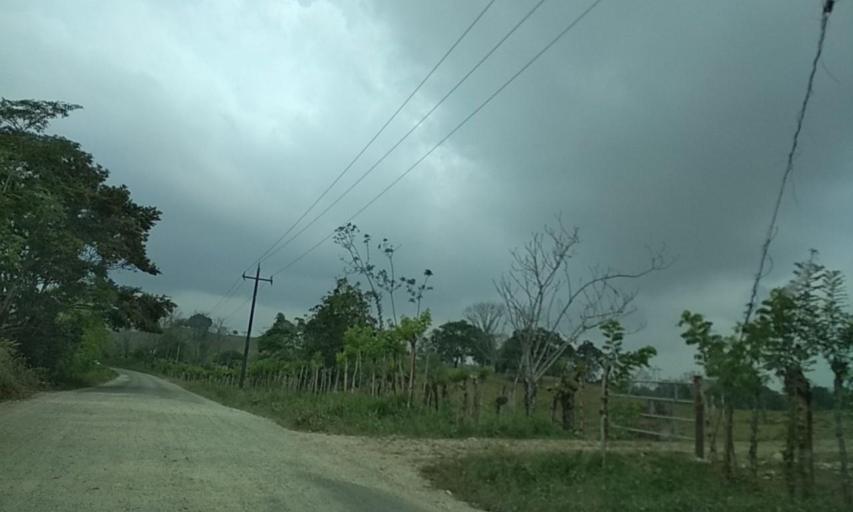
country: MX
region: Tabasco
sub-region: Huimanguillo
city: Francisco Rueda
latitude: 17.6065
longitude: -94.0926
